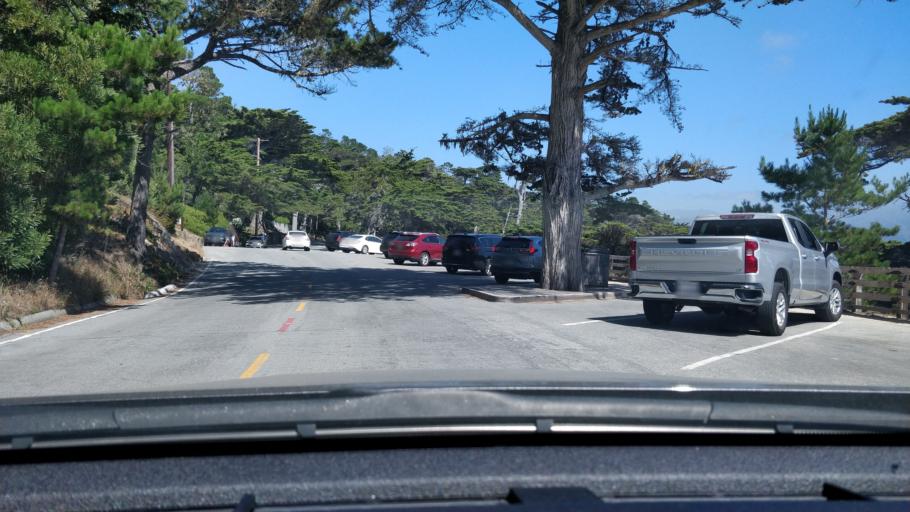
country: US
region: California
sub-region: Monterey County
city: Del Monte Forest
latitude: 36.5697
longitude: -121.9660
